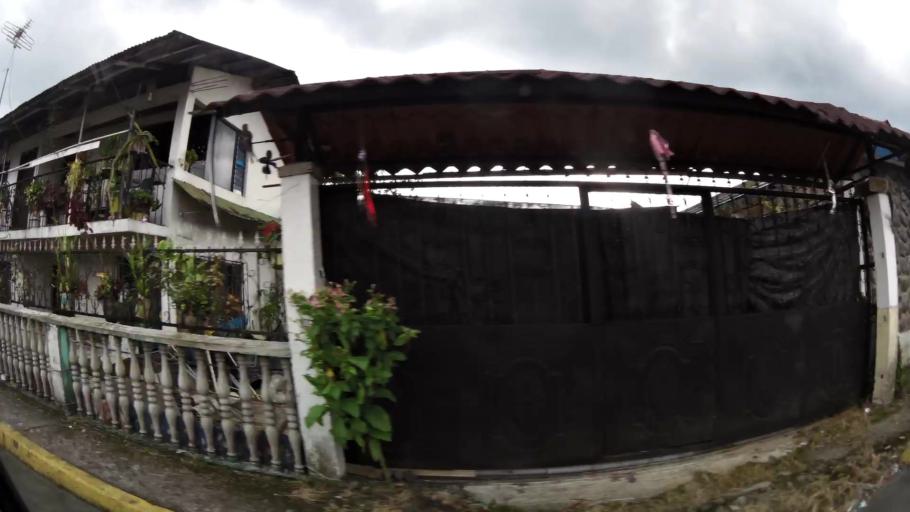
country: EC
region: Pastaza
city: Puyo
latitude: -1.4623
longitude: -78.1125
